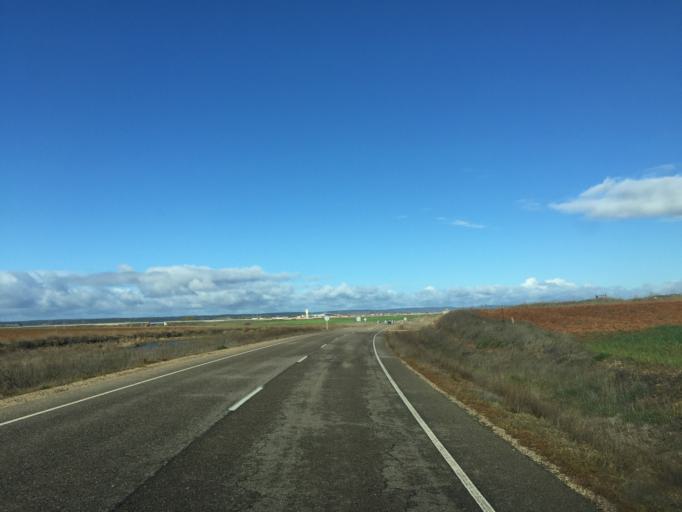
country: ES
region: Castille and Leon
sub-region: Provincia de Zamora
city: Manganeses de la Lampreana
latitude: 41.7601
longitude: -5.7422
